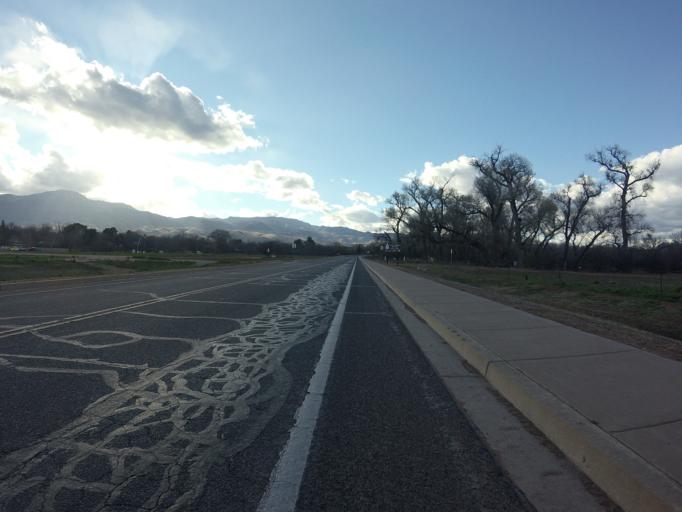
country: US
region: Arizona
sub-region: Yavapai County
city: Cottonwood
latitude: 34.7479
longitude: -112.0179
